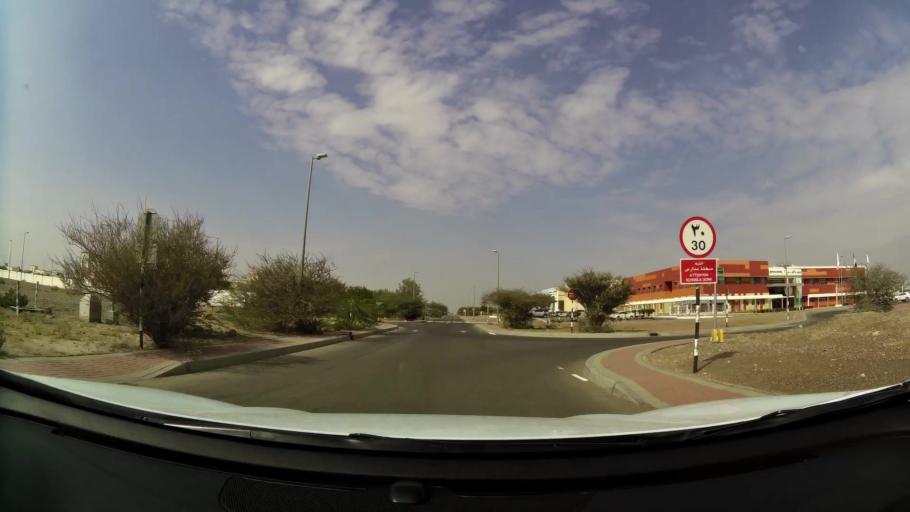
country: AE
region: Abu Dhabi
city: Al Ain
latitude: 24.0984
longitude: 55.9049
